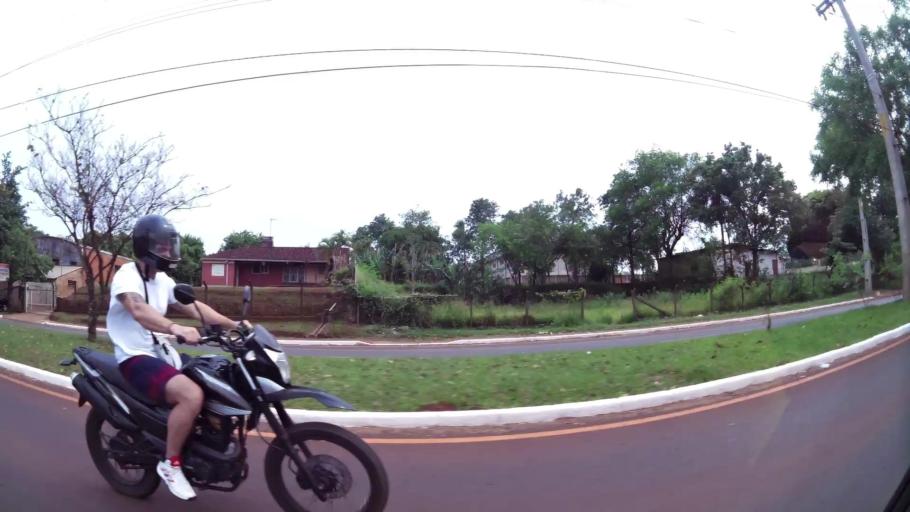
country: PY
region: Alto Parana
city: Presidente Franco
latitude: -25.5486
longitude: -54.6205
